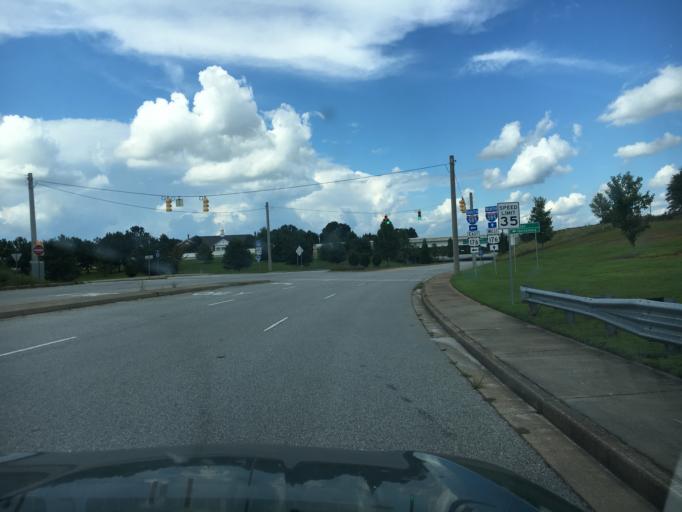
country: US
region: South Carolina
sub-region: Spartanburg County
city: Southern Shops
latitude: 34.9916
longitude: -81.9723
